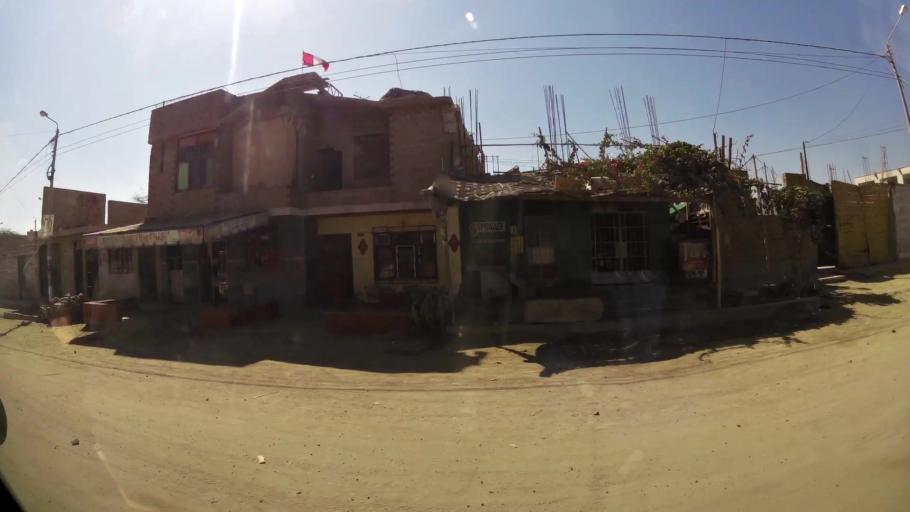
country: PE
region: Ica
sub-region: Provincia de Ica
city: La Tinguina
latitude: -14.0386
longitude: -75.7030
